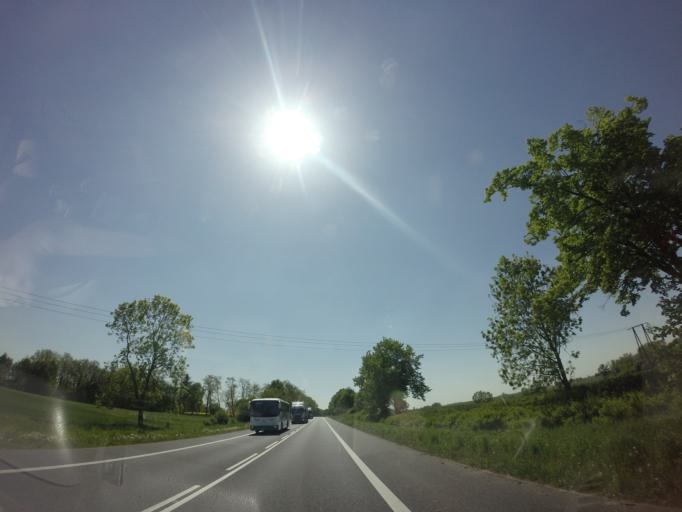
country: PL
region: West Pomeranian Voivodeship
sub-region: Powiat pyrzycki
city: Lipiany
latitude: 52.9814
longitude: 14.9774
